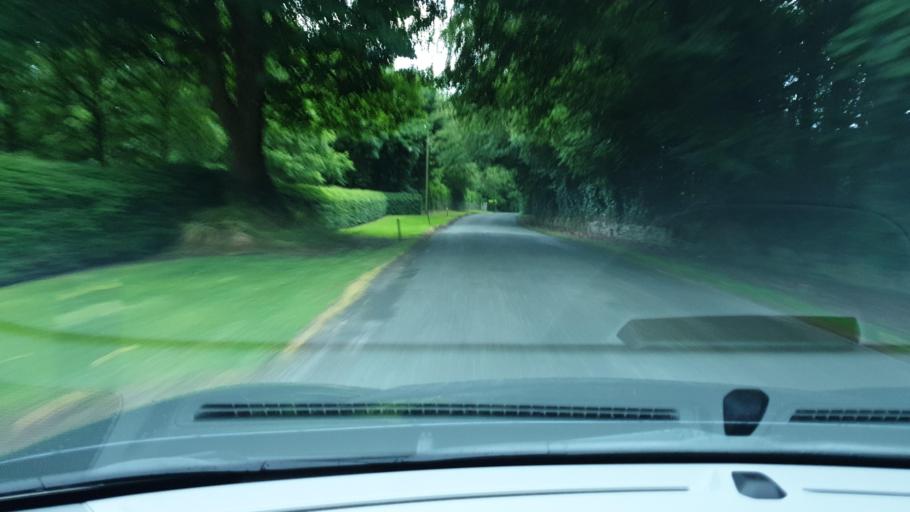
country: IE
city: Kentstown
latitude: 53.6009
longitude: -6.5986
